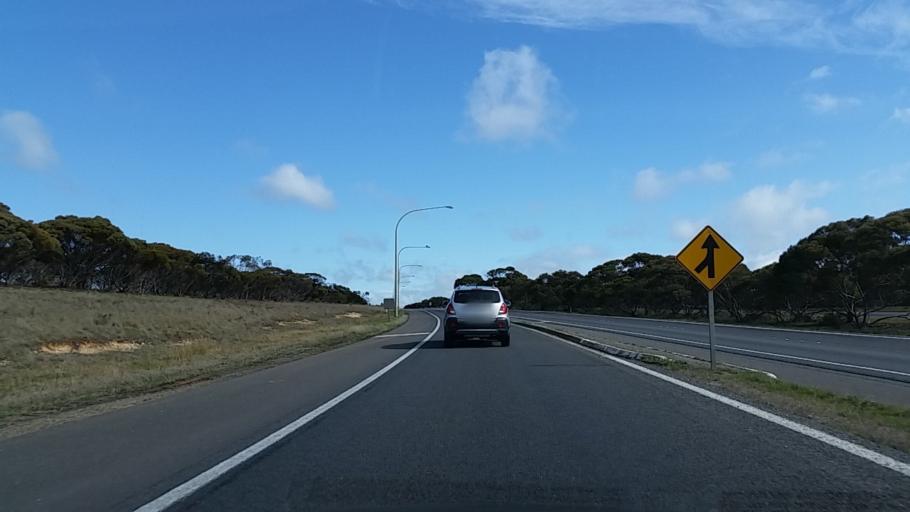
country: AU
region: South Australia
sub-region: Murray Bridge
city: Murray Bridge
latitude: -35.1459
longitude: 139.2229
